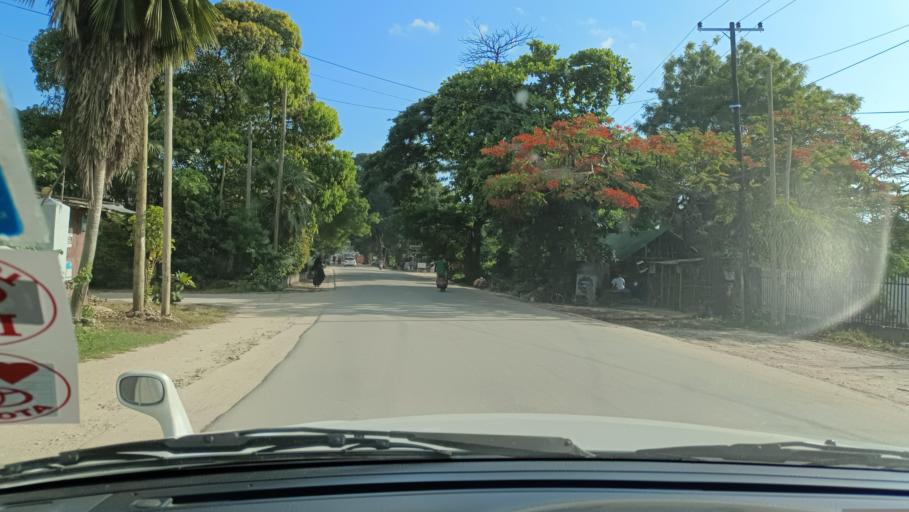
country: TZ
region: Zanzibar Urban/West
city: Zanzibar
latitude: -6.2032
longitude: 39.2090
